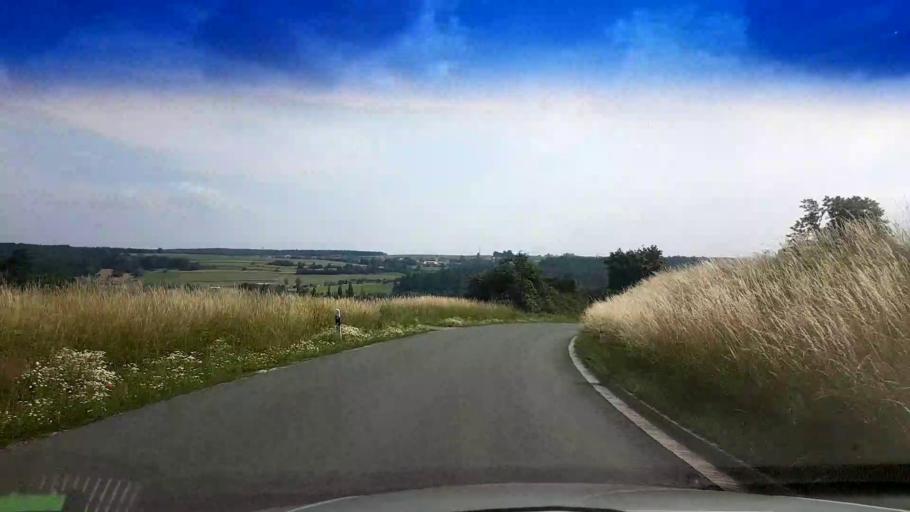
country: DE
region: Bavaria
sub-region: Upper Franconia
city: Priesendorf
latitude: 49.9002
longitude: 10.7321
